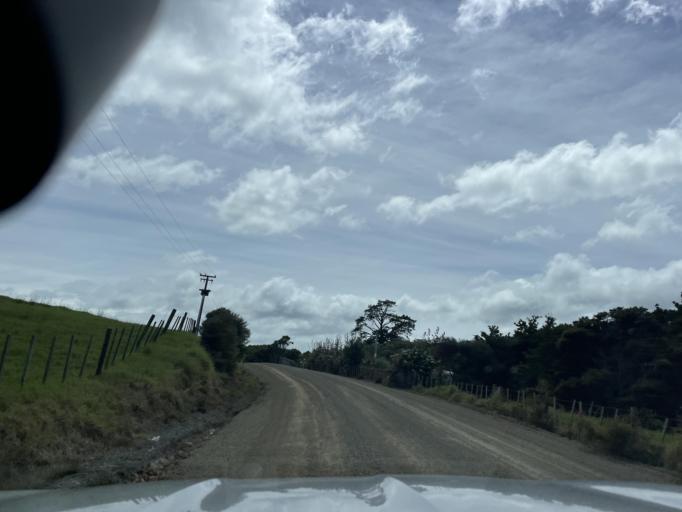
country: NZ
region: Auckland
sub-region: Auckland
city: Wellsford
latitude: -36.1550
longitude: 174.2873
